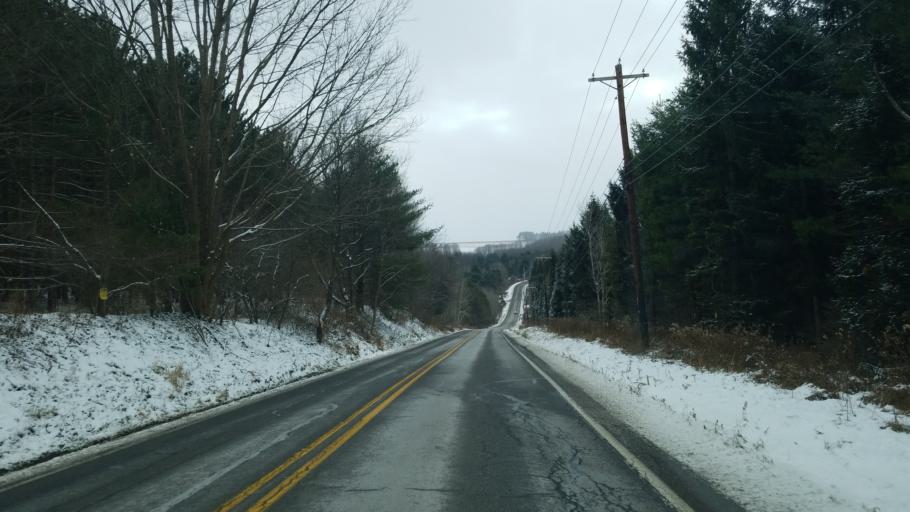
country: US
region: Pennsylvania
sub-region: Clearfield County
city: Sandy
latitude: 41.0810
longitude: -78.7353
